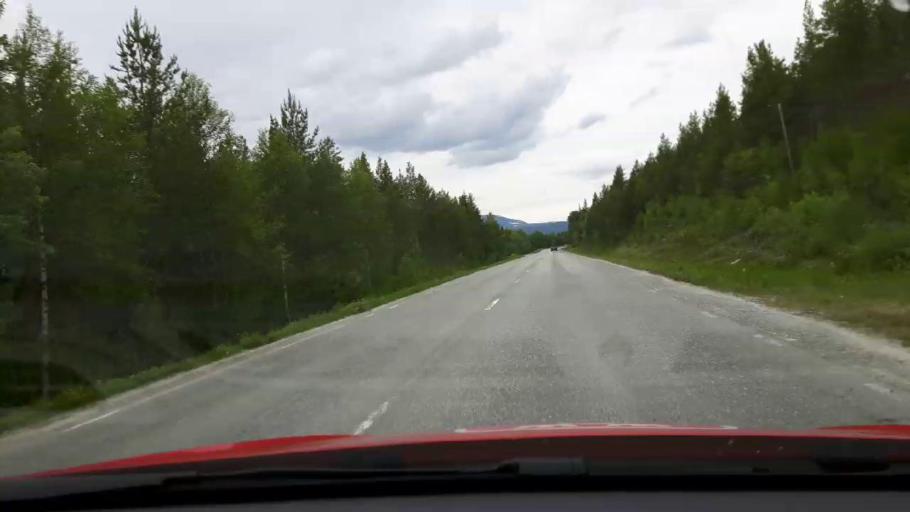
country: NO
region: Hedmark
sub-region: Engerdal
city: Engerdal
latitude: 62.5321
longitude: 12.5648
